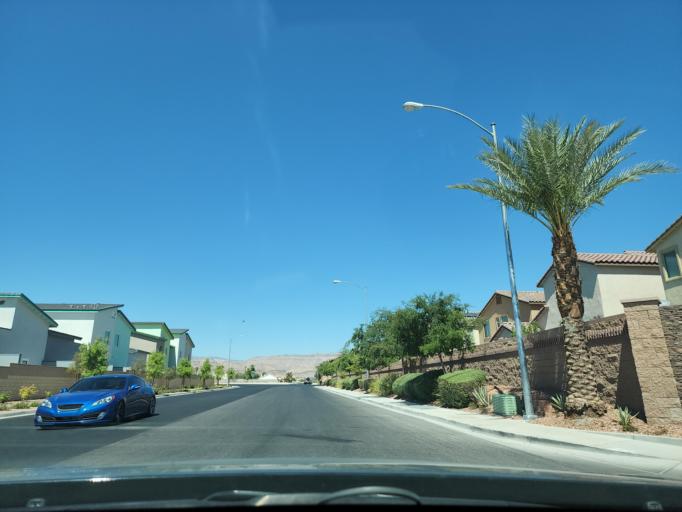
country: US
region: Nevada
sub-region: Clark County
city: Spring Valley
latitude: 36.0812
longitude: -115.2594
